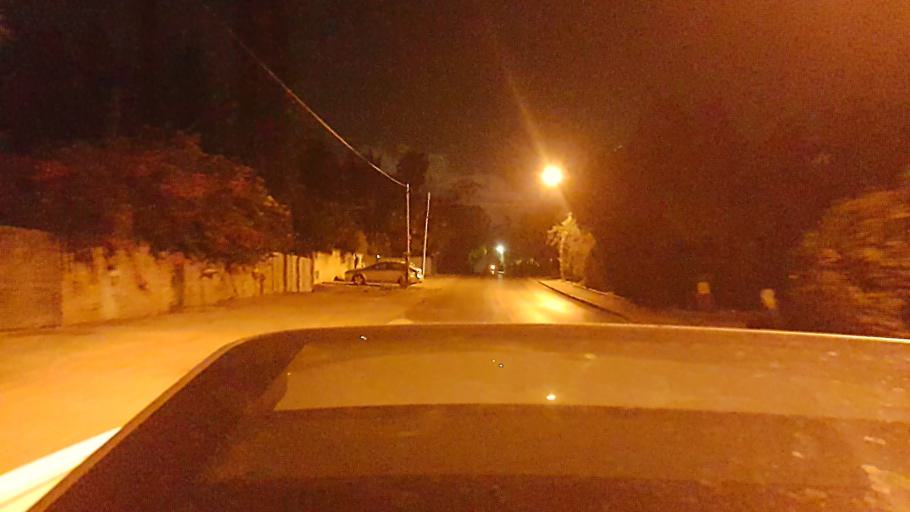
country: IL
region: Central District
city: Hod HaSharon
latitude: 32.1625
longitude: 34.8826
